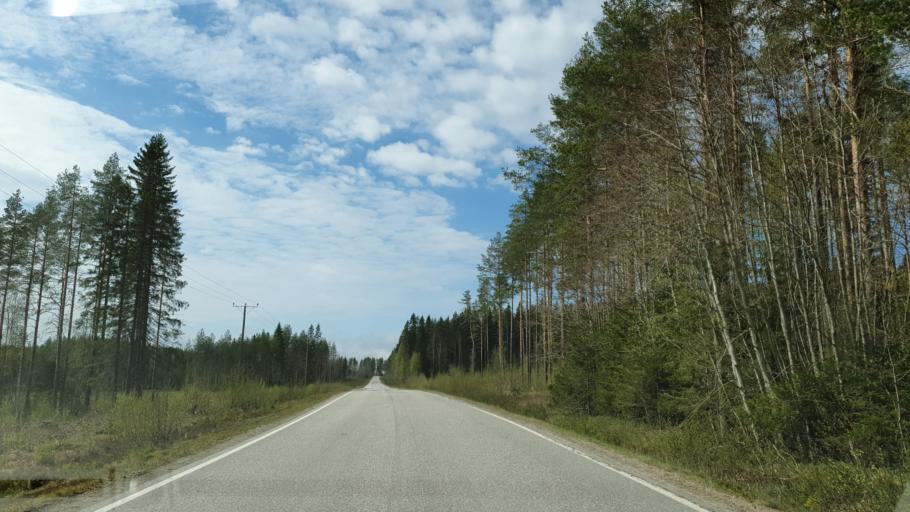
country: FI
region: Kainuu
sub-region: Kehys-Kainuu
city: Kuhmo
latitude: 64.1212
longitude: 29.6832
